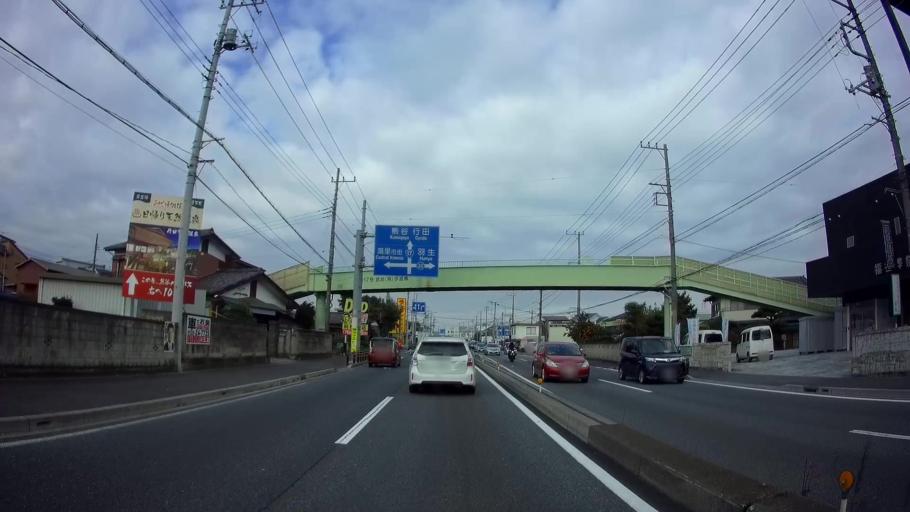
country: JP
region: Saitama
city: Konosu
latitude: 36.0661
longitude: 139.5128
